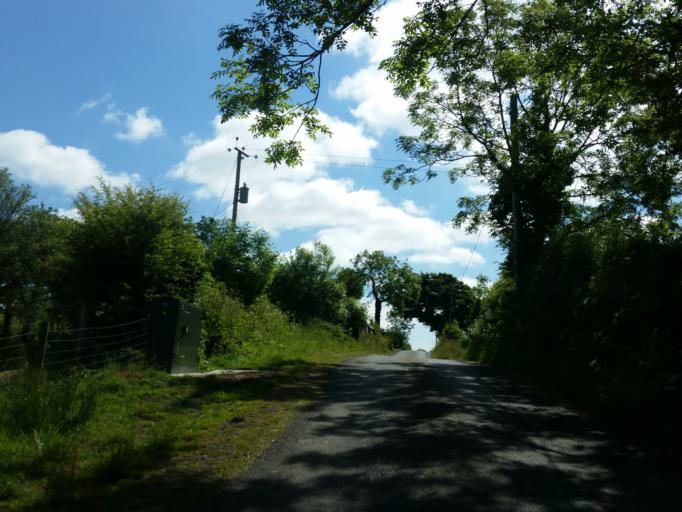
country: GB
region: Northern Ireland
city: Ballinamallard
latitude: 54.3205
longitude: -7.5562
